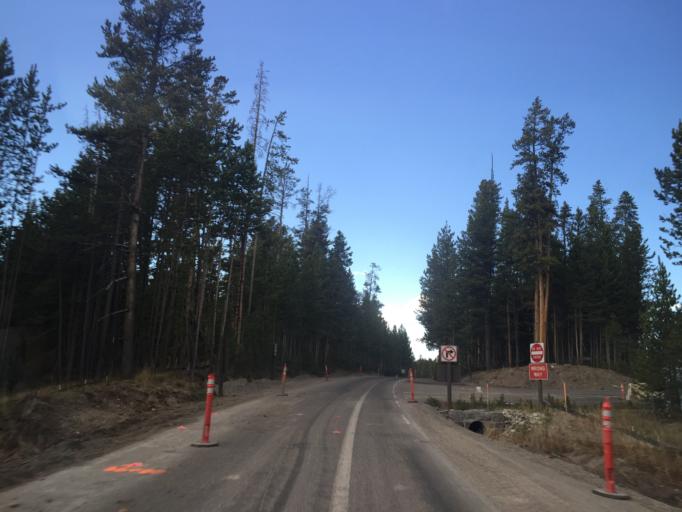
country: US
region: Montana
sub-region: Gallatin County
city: West Yellowstone
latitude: 44.7343
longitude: -110.4869
